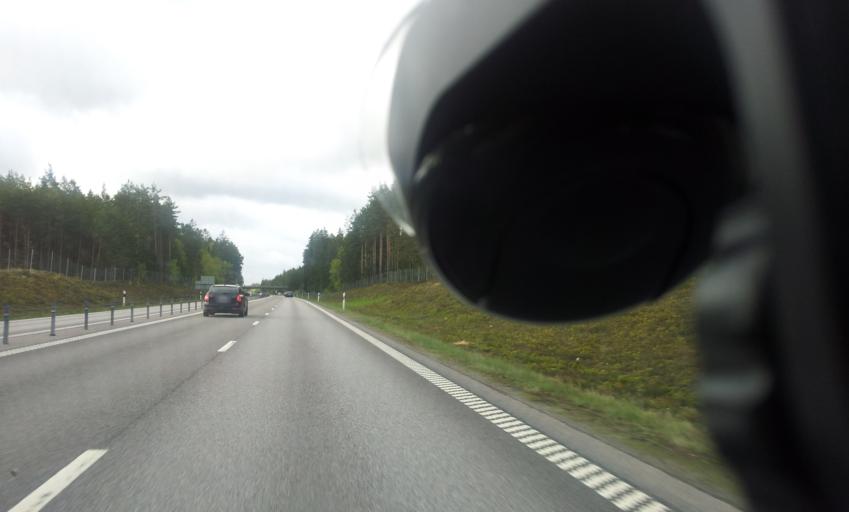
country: SE
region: Kalmar
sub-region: Kalmar Kommun
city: Ljungbyholm
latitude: 56.5399
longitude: 16.0838
